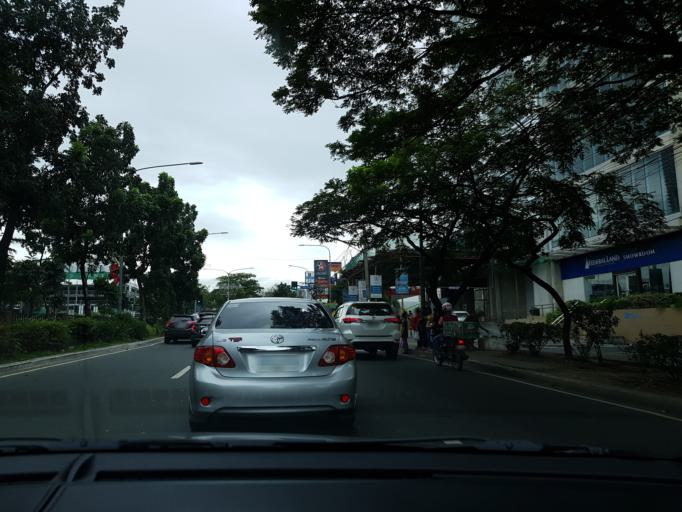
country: PH
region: Metro Manila
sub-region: San Juan
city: San Juan
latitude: 14.6015
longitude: 121.0473
